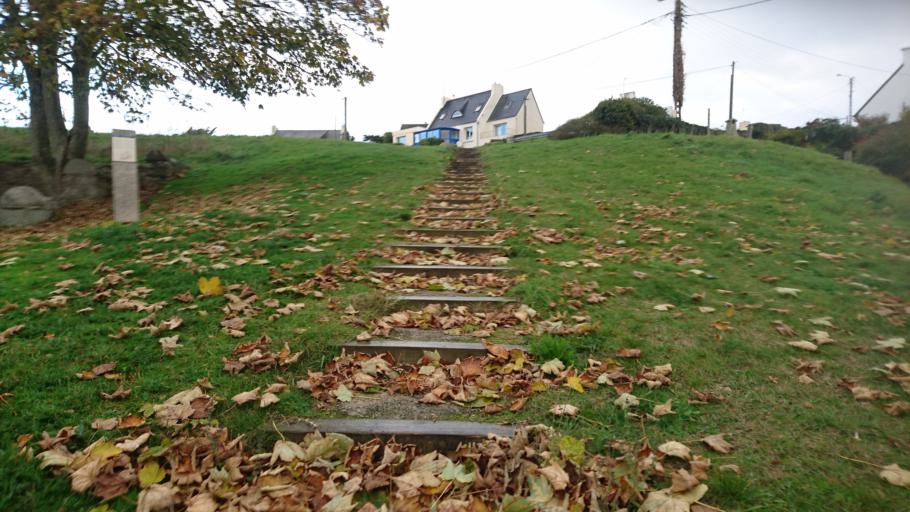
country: FR
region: Brittany
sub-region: Departement du Finistere
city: Lampaul-Plouarzel
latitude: 48.4442
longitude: -4.7706
